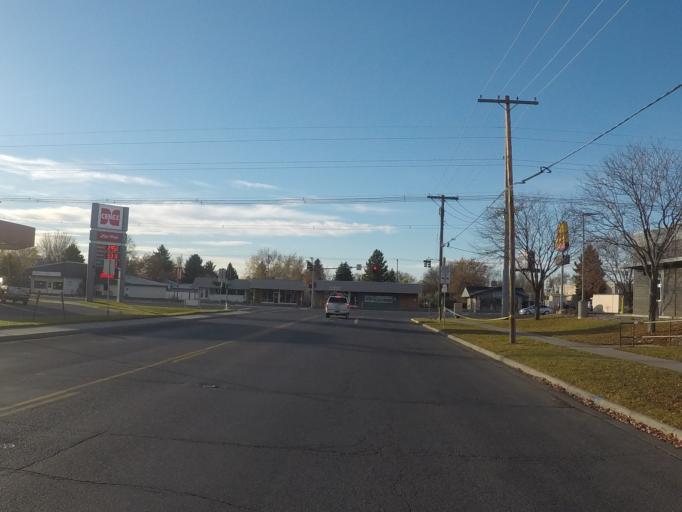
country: US
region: Montana
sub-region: Yellowstone County
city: Billings
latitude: 45.7848
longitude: -108.5903
